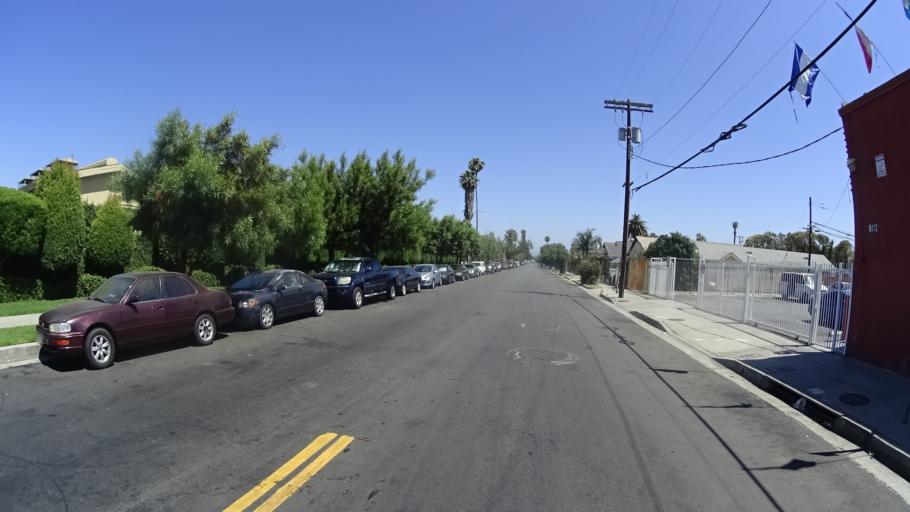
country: US
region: California
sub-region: Los Angeles County
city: Los Angeles
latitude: 34.0257
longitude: -118.2959
